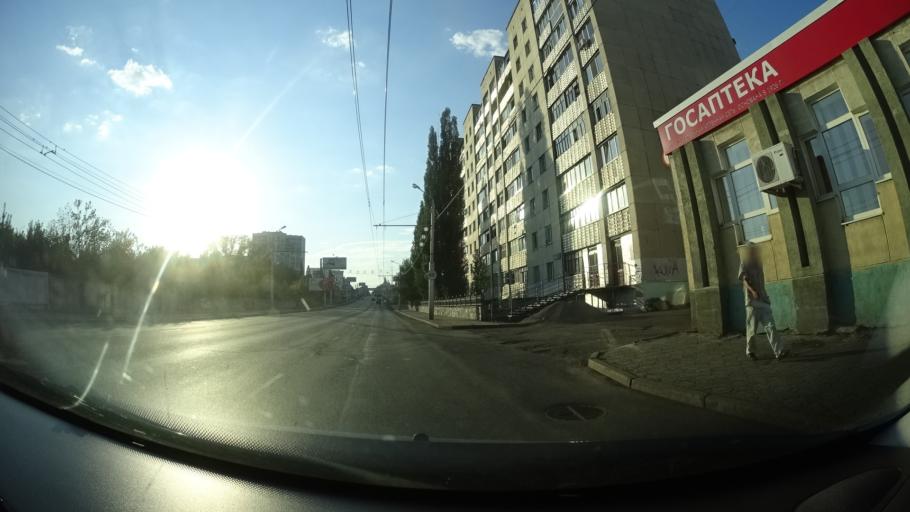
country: RU
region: Bashkortostan
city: Sterlitamak
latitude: 53.6215
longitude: 55.9563
